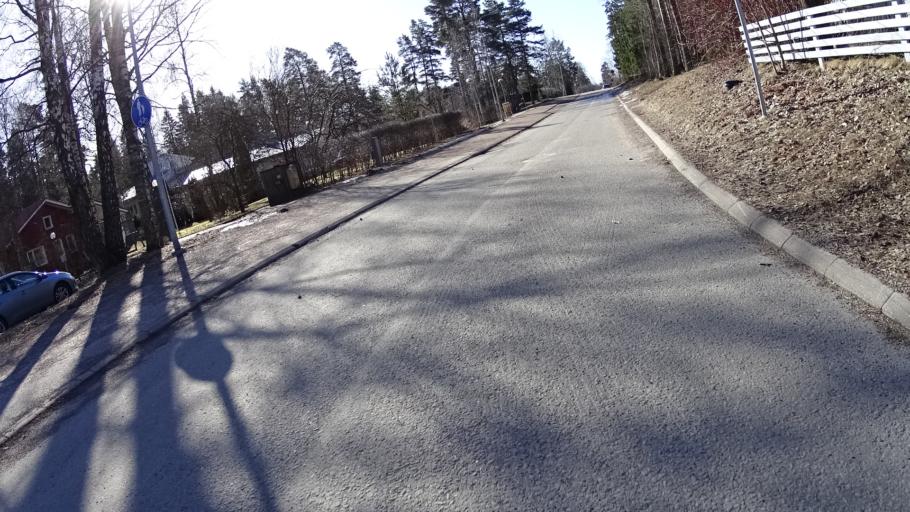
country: FI
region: Uusimaa
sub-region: Helsinki
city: Kilo
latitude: 60.2067
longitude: 24.8050
